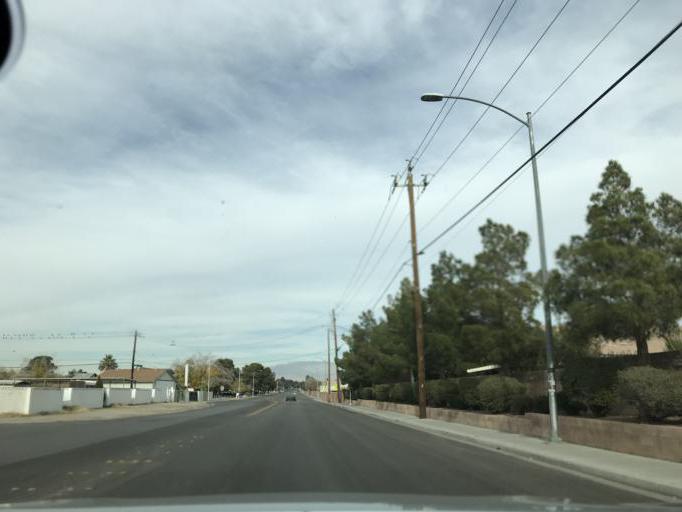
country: US
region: Nevada
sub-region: Clark County
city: Las Vegas
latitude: 36.2091
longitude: -115.2156
